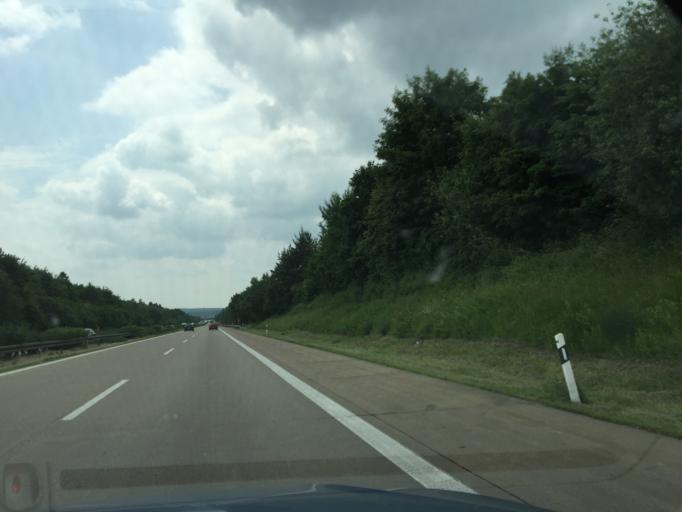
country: DE
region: Baden-Wuerttemberg
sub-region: Regierungsbezirk Stuttgart
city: Ellenberg
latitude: 49.0770
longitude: 10.2006
